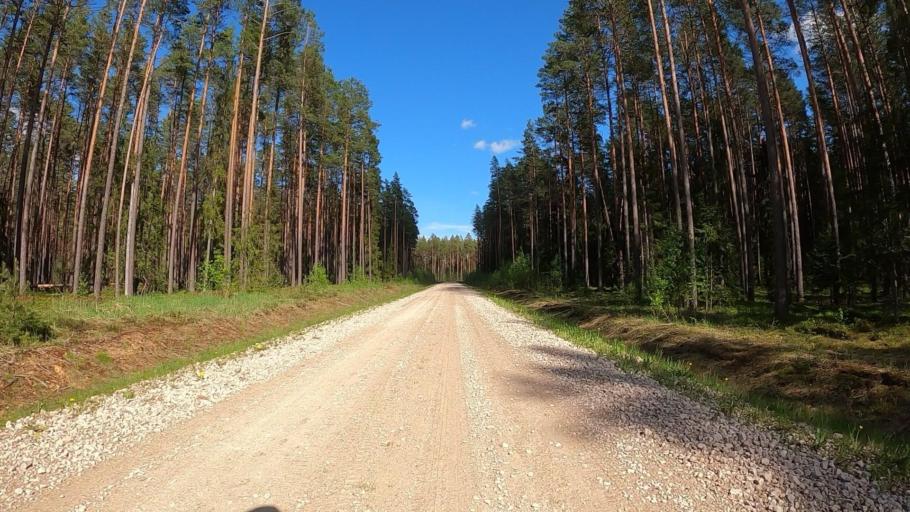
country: LV
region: Baldone
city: Baldone
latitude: 56.7836
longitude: 24.3682
